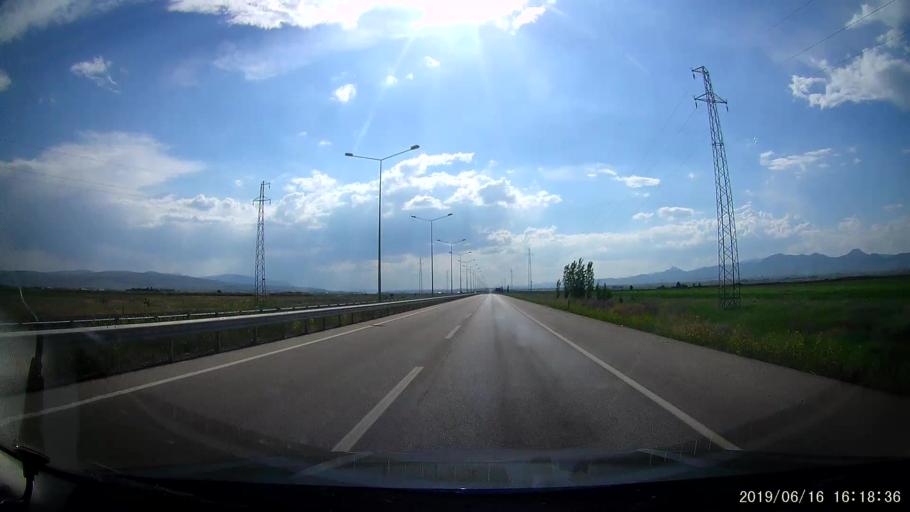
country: TR
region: Erzurum
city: Ilica
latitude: 39.9652
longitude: 41.1642
